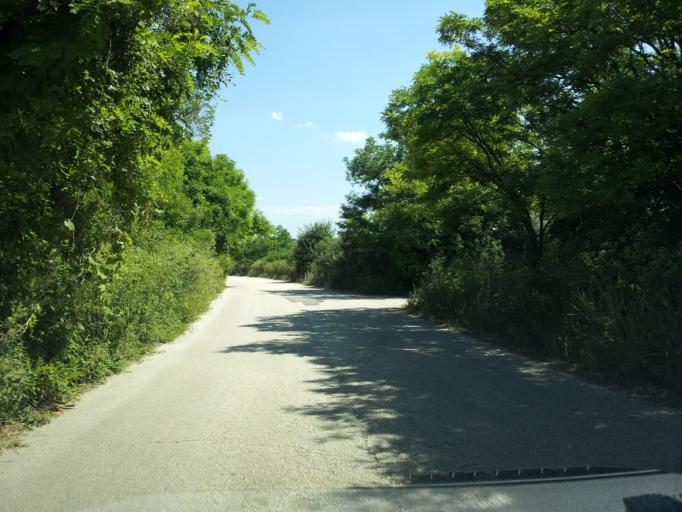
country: HU
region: Fejer
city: Szarliget
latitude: 47.5267
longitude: 18.5721
